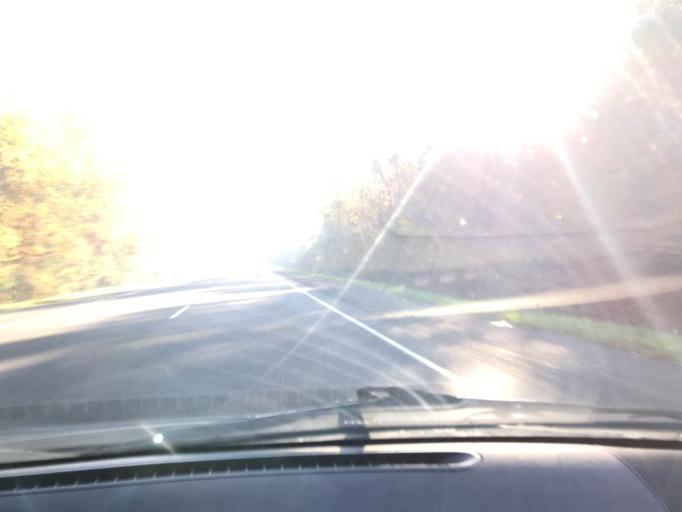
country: BY
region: Brest
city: Horad Luninyets
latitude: 52.2962
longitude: 26.7454
